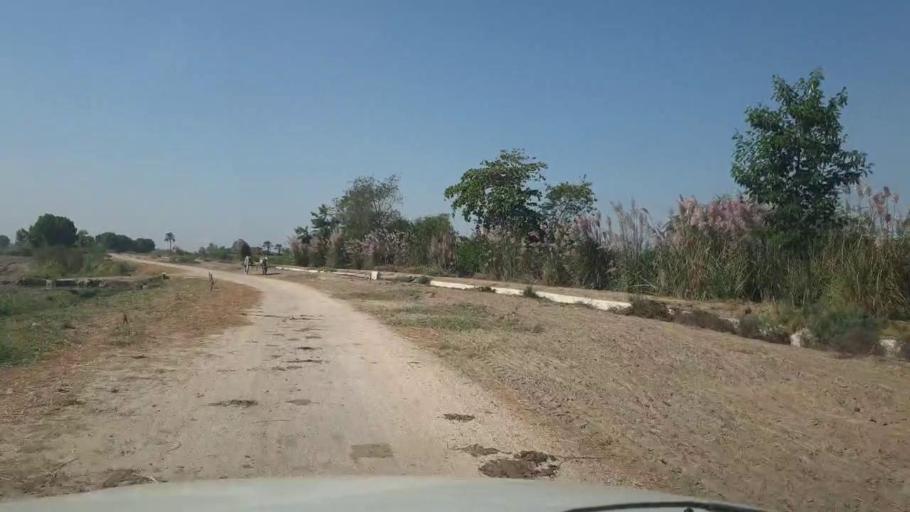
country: PK
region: Sindh
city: Mirpur Sakro
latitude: 24.4197
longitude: 67.7871
